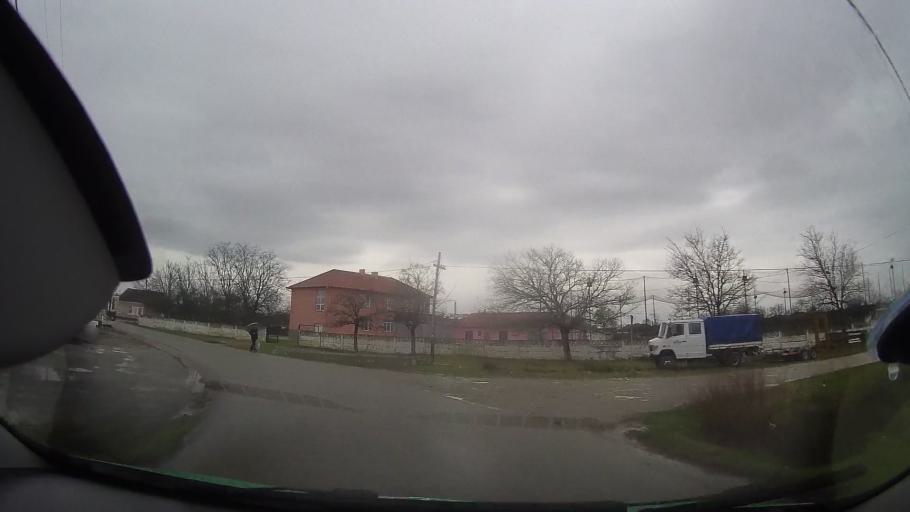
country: RO
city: Capalna
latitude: 46.7377
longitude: 22.1018
